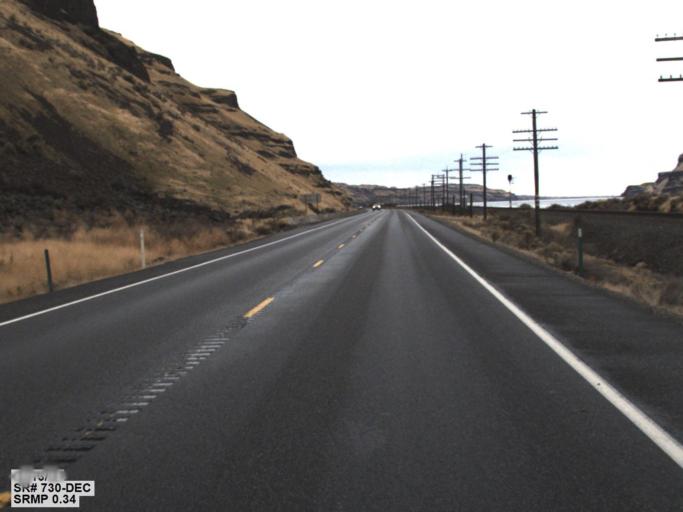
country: US
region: Washington
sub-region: Benton County
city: Finley
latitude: 46.0043
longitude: -118.9712
